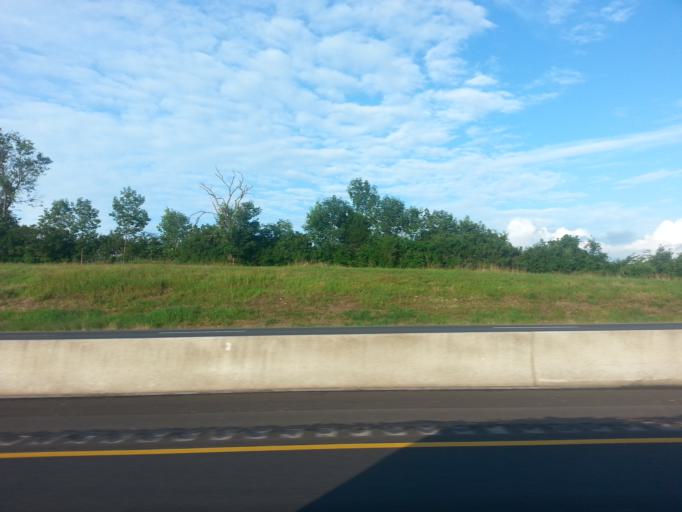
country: US
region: Kentucky
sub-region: Madison County
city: Richmond
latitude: 37.6981
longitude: -84.3171
